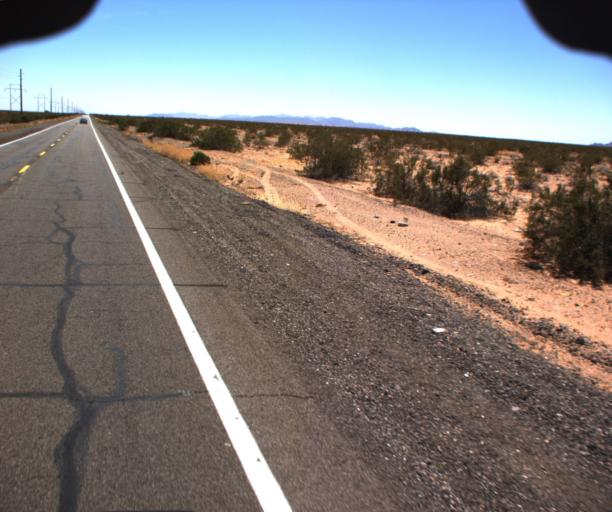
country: US
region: Arizona
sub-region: La Paz County
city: Parker
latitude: 33.9221
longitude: -114.2169
